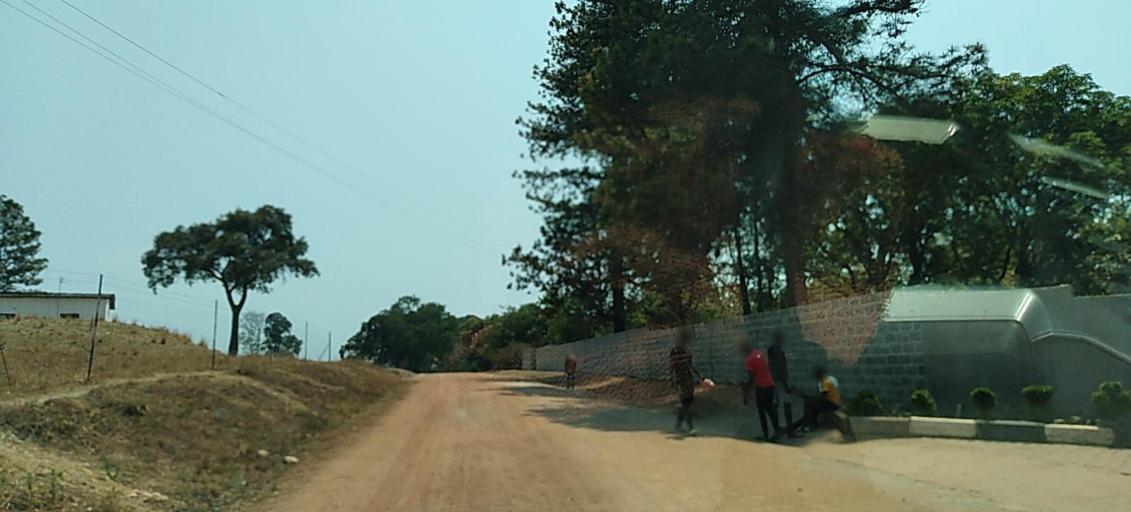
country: ZM
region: Copperbelt
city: Chingola
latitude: -12.6250
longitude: 27.9412
